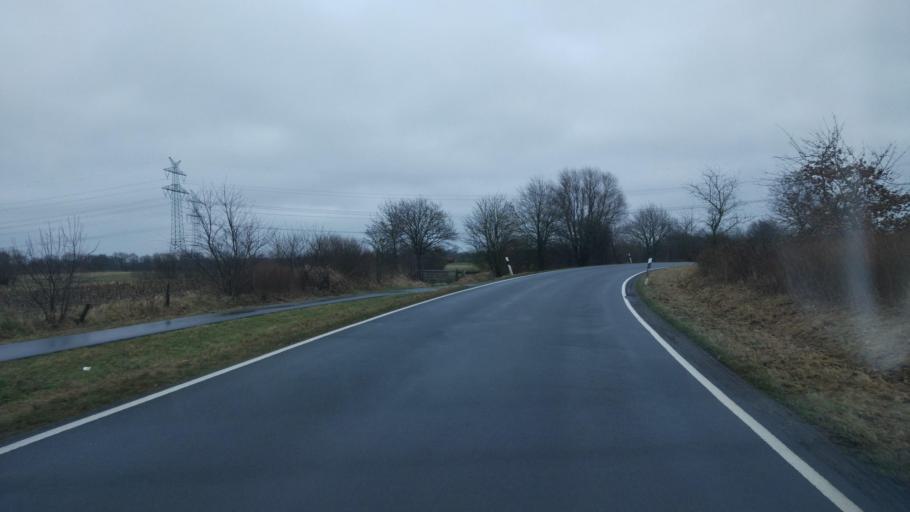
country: DE
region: Schleswig-Holstein
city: Ellingstedt
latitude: 54.4702
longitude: 9.4187
